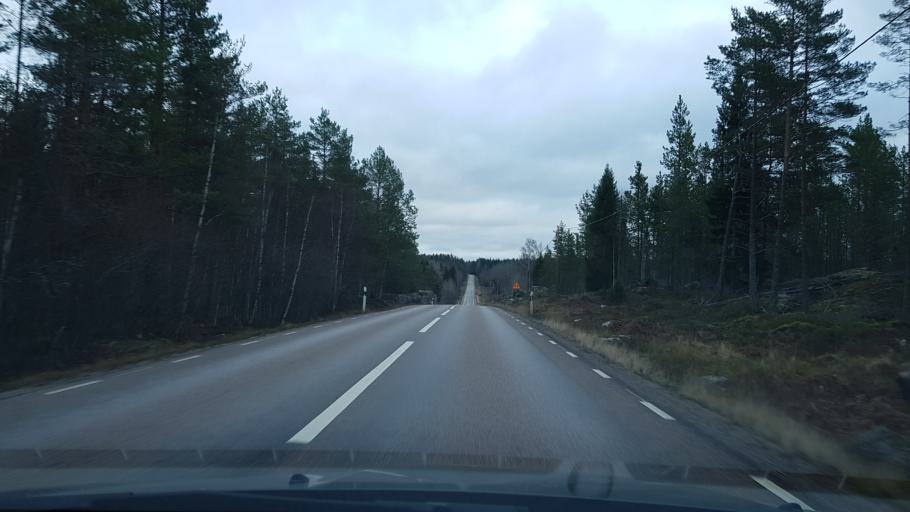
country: SE
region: Uppsala
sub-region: Osthammars Kommun
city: Gimo
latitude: 59.9838
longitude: 18.2292
